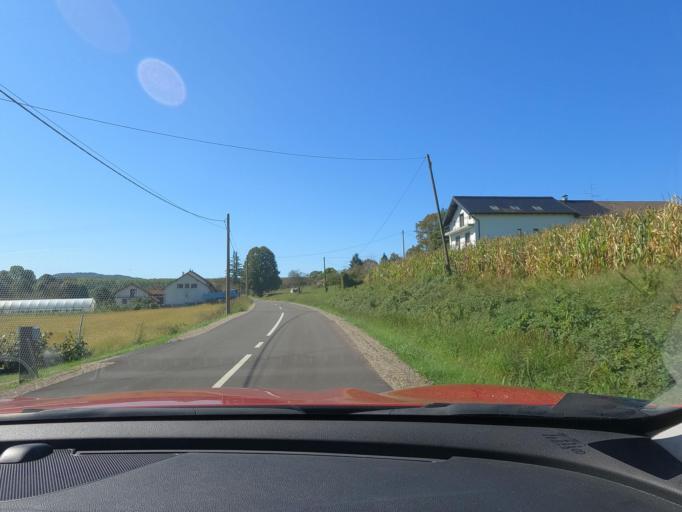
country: HR
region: Sisacko-Moslavacka
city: Petrinja
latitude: 45.4566
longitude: 16.2632
